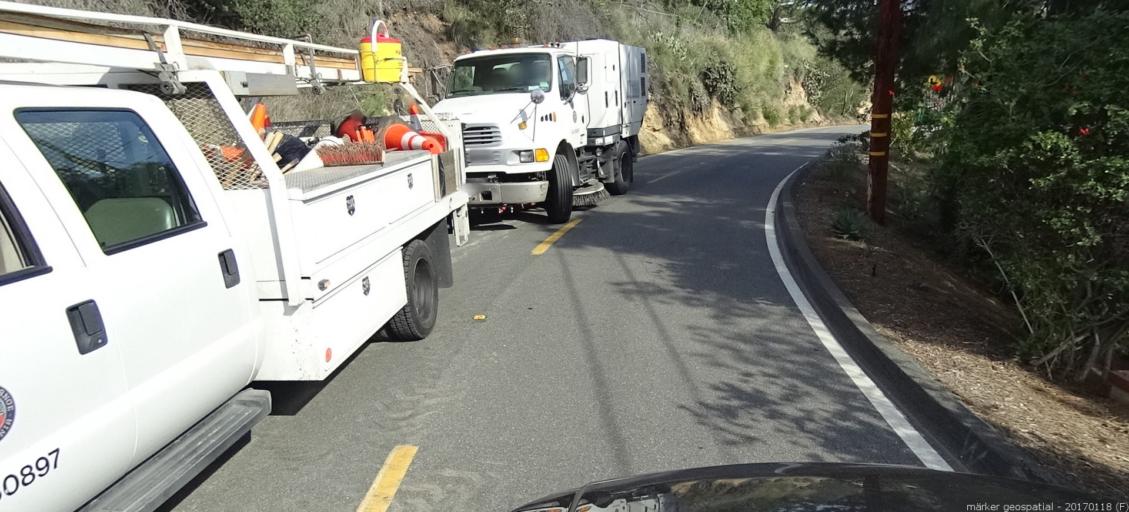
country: US
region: California
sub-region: Orange County
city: North Tustin
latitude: 33.7561
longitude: -117.7777
